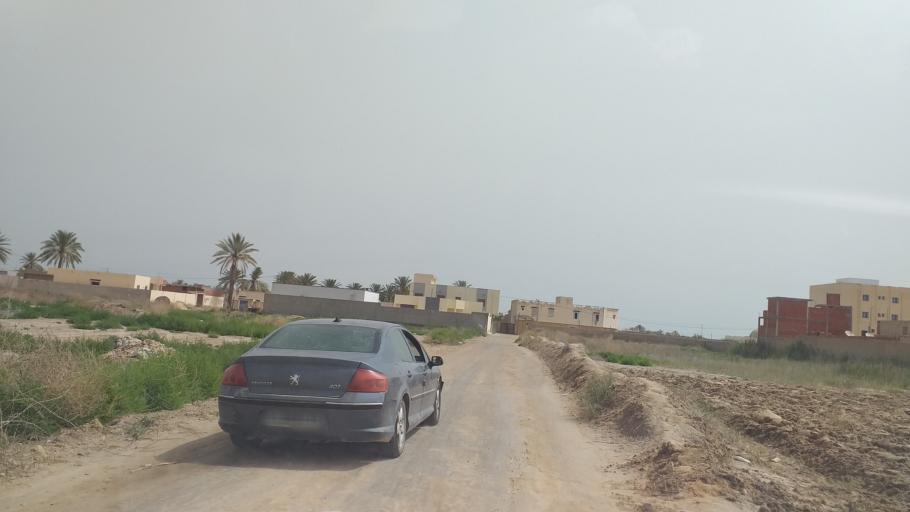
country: TN
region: Qabis
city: Gabes
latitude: 33.9425
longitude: 10.0557
